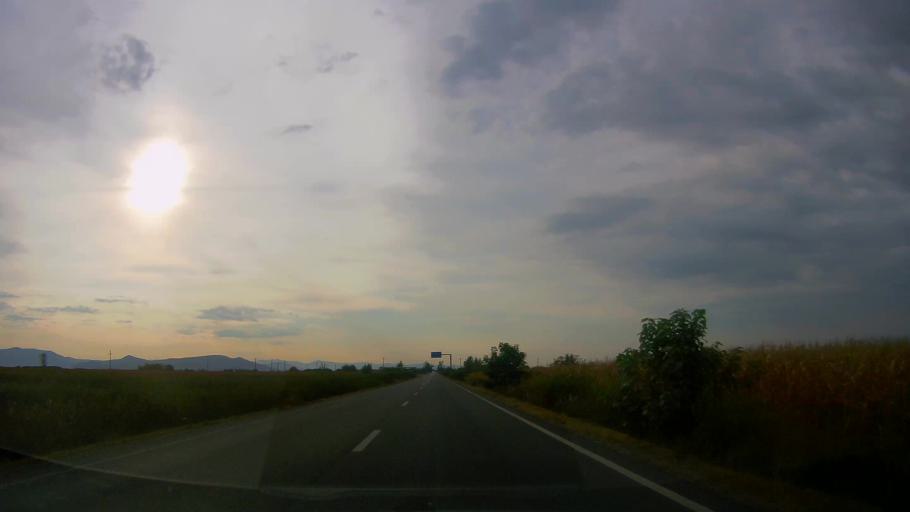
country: RO
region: Satu Mare
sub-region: Comuna Halmeu
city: Halmeu
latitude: 47.9602
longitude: 23.0512
